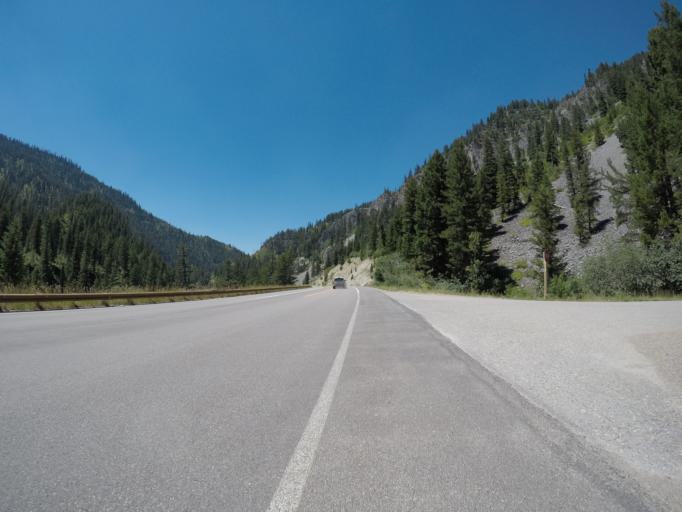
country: US
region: Wyoming
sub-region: Teton County
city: Hoback
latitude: 43.1985
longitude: -110.9033
